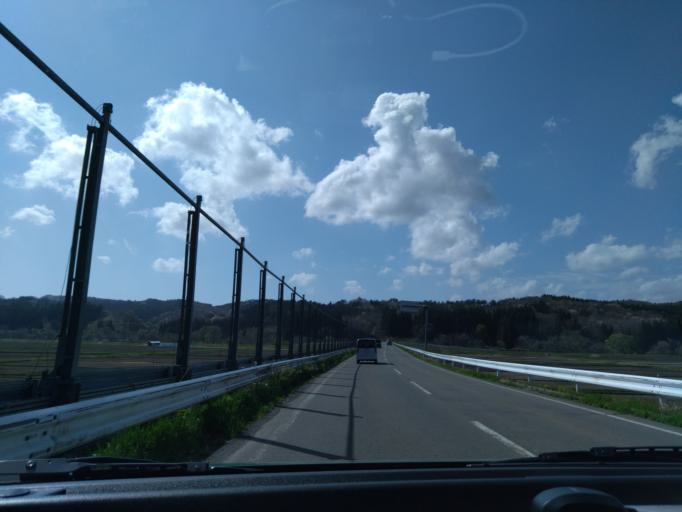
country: JP
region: Akita
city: Akita
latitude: 39.6935
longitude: 140.2730
